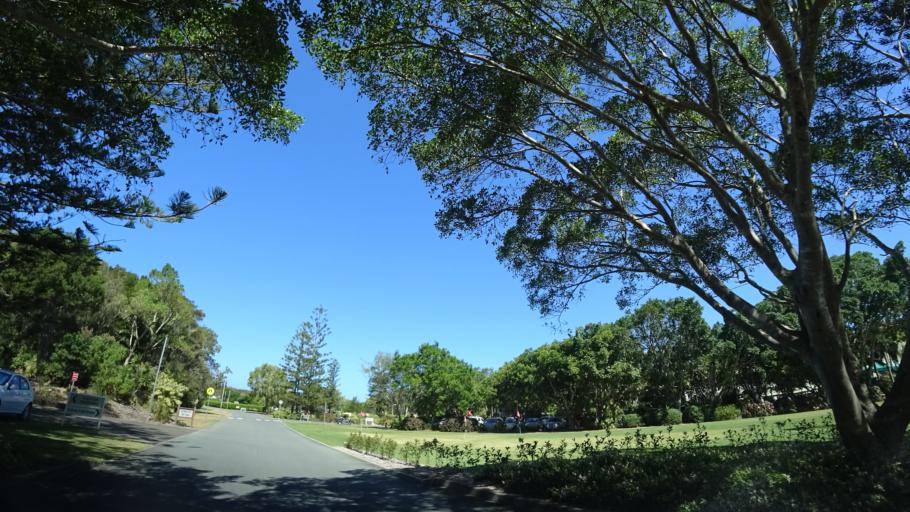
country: AU
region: Queensland
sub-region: Sunshine Coast
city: Mooloolaba
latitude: -26.6311
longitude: 153.0974
